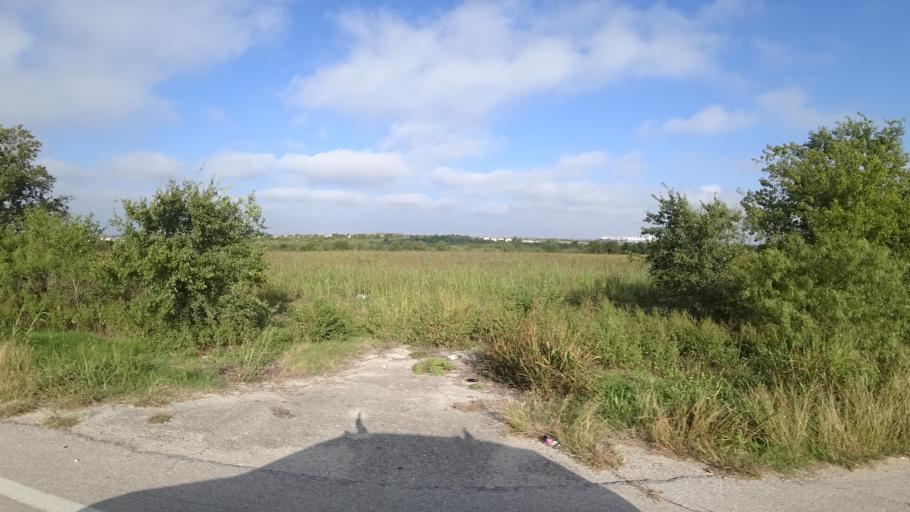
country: US
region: Texas
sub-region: Travis County
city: Manor
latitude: 30.3582
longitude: -97.6328
